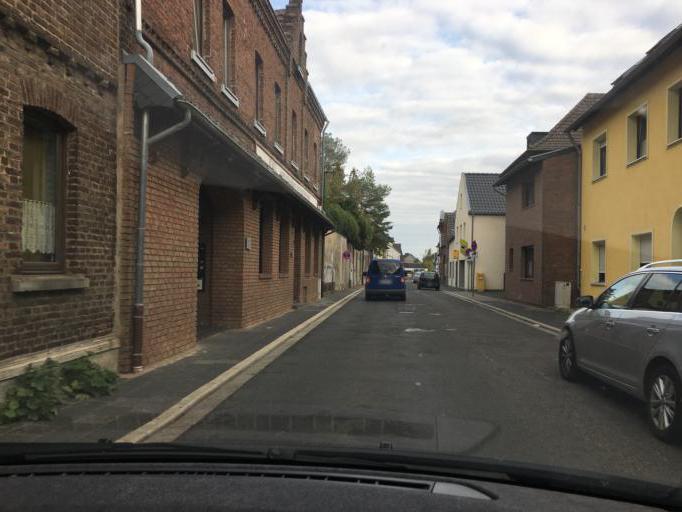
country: DE
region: North Rhine-Westphalia
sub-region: Regierungsbezirk Koln
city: Merzenich
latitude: 50.8588
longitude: 6.5842
